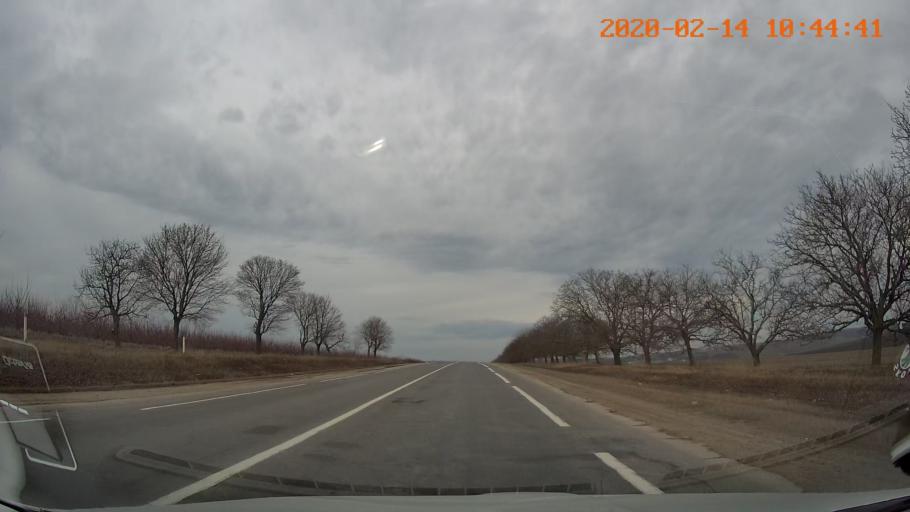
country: MD
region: Riscani
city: Riscani
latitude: 48.0231
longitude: 27.5488
